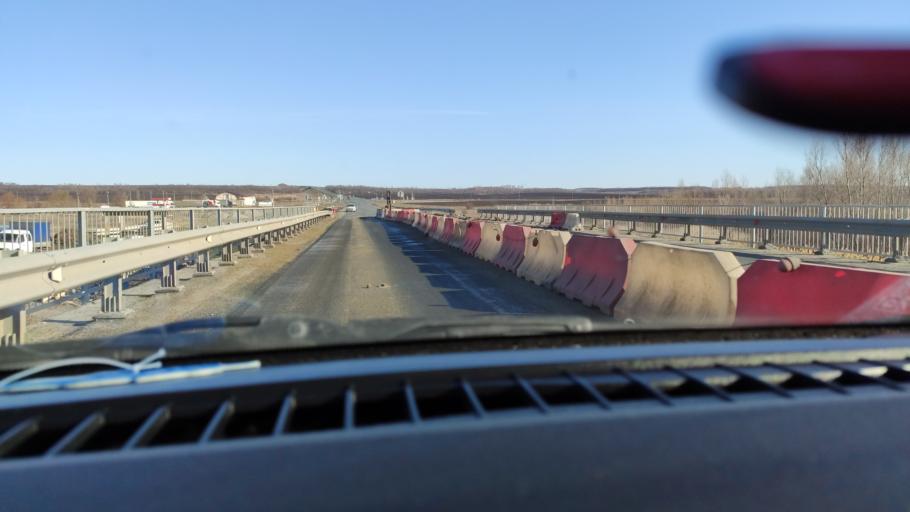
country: RU
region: Saratov
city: Dukhovnitskoye
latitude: 52.7387
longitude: 48.2548
